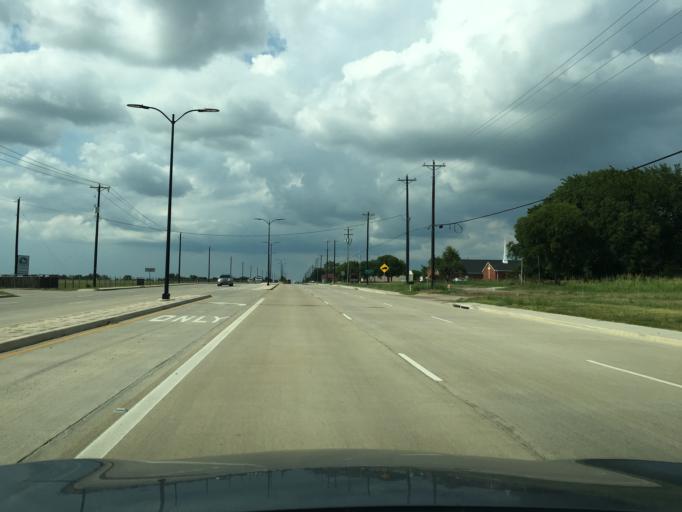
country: US
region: Texas
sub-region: Denton County
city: Oak Point
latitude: 33.1689
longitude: -96.9771
